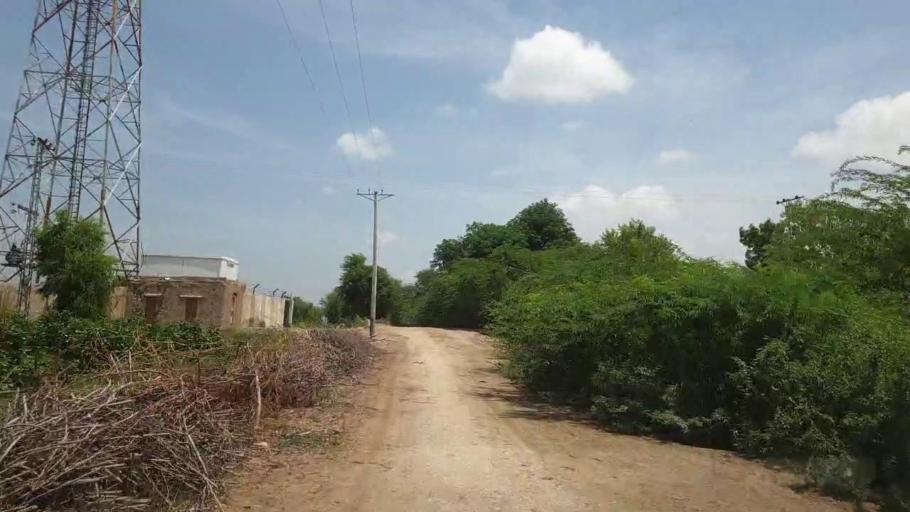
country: PK
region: Sindh
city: Kot Diji
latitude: 27.1474
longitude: 69.0162
